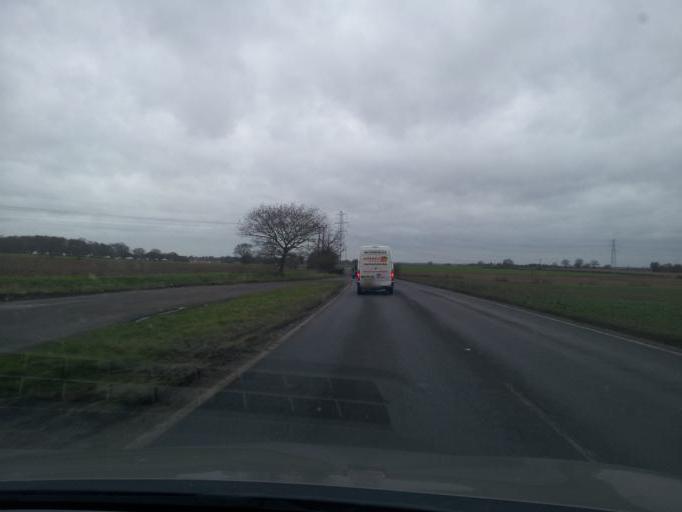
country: GB
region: England
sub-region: Suffolk
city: Ixworth
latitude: 52.3287
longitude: 0.9093
